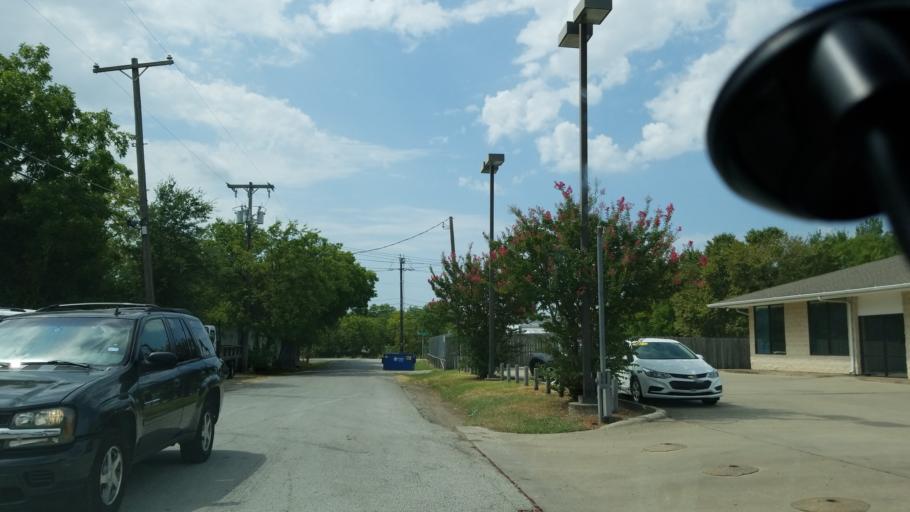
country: US
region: Texas
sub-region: Dallas County
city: Grand Prairie
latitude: 32.7462
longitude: -96.9912
